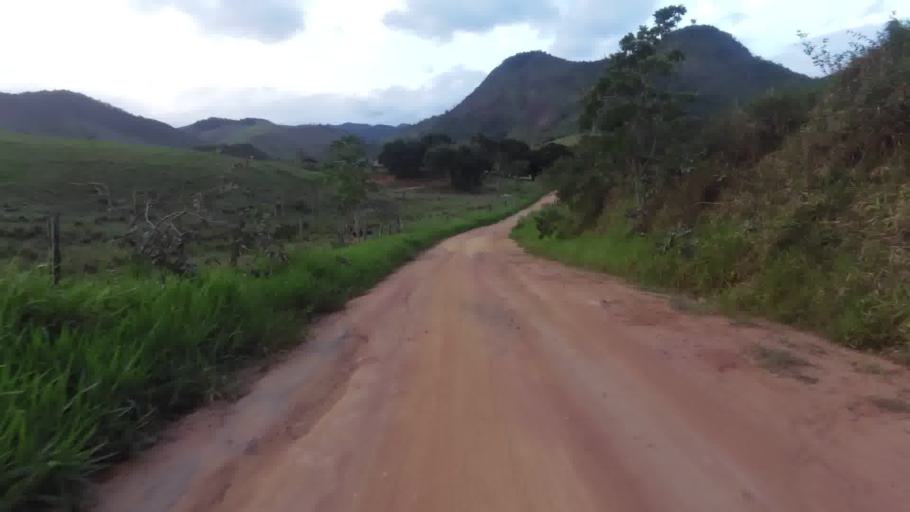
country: BR
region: Espirito Santo
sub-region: Guarapari
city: Guarapari
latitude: -20.6661
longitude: -40.6089
